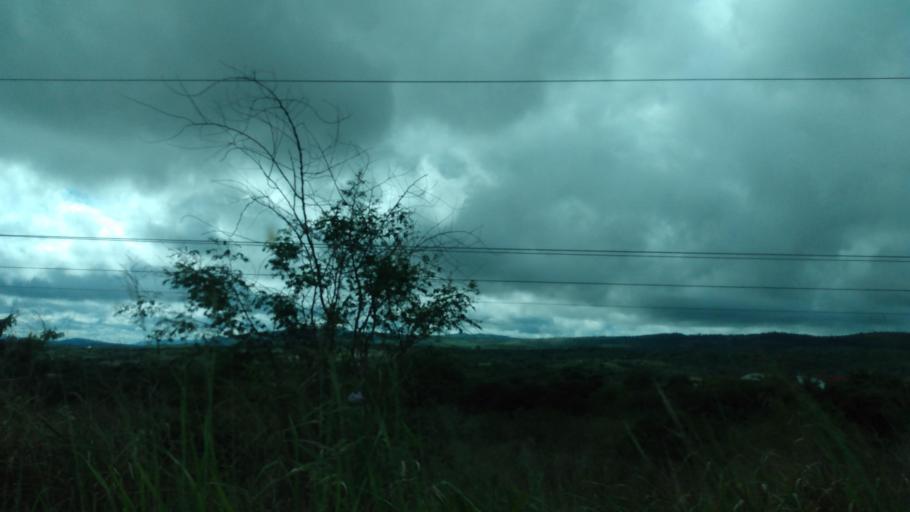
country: BR
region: Pernambuco
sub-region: Caruaru
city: Caruaru
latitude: -8.3236
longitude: -35.9816
